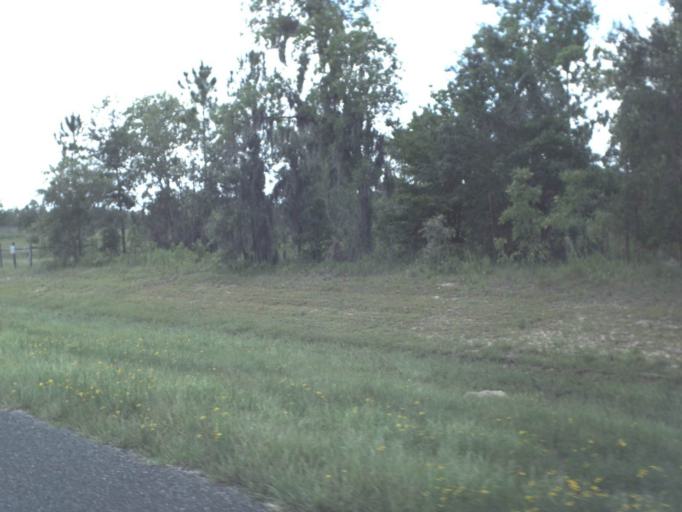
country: US
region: Florida
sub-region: Levy County
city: East Bronson
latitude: 29.4183
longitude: -82.5657
